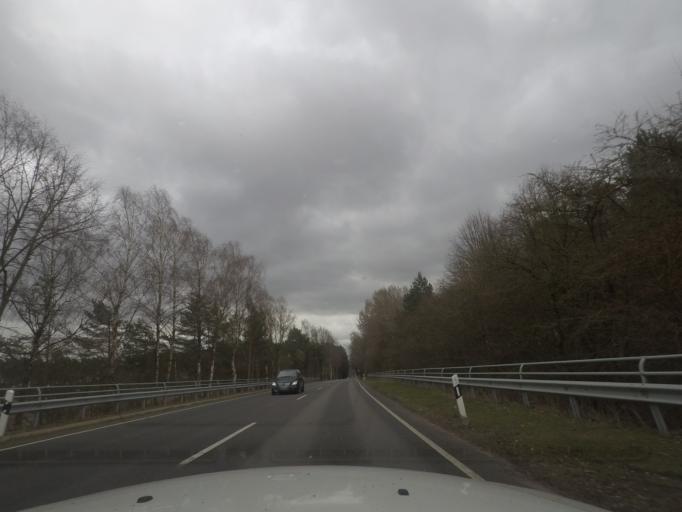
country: DE
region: Lower Saxony
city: Bad Bevensen
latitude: 53.0640
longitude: 10.6033
